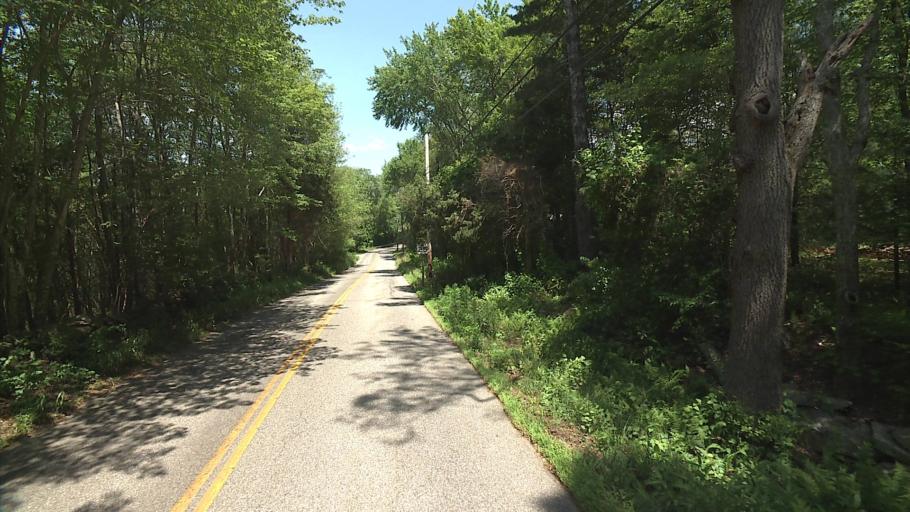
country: US
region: Connecticut
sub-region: New London County
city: Preston City
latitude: 41.5421
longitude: -71.8822
